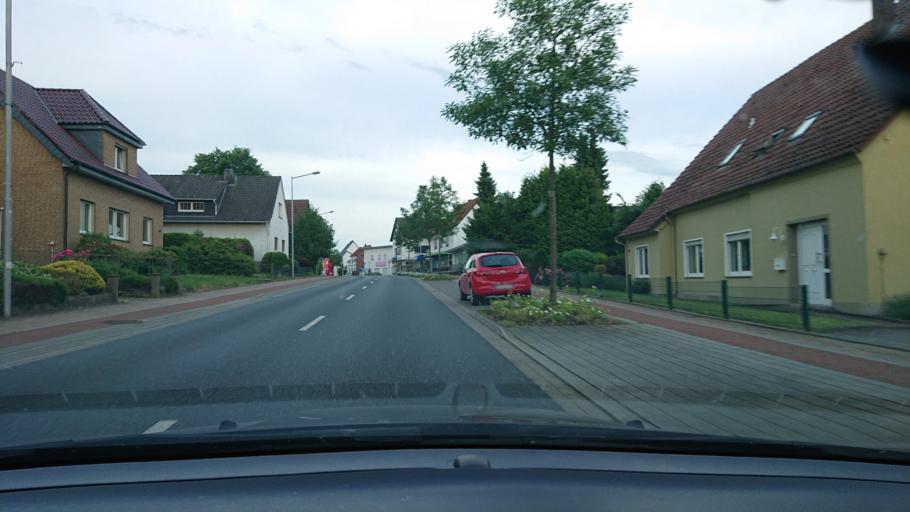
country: DE
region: North Rhine-Westphalia
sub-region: Regierungsbezirk Detmold
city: Hiddenhausen
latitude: 52.1686
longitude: 8.6272
